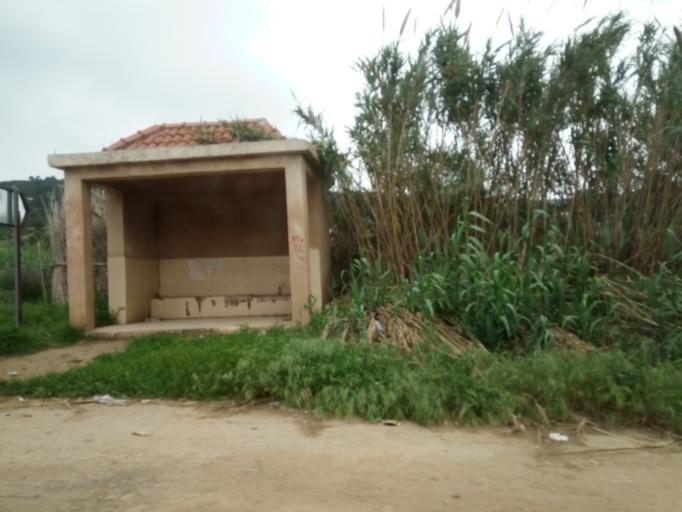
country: DZ
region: Tipaza
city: Tipasa
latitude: 36.5899
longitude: 2.5206
